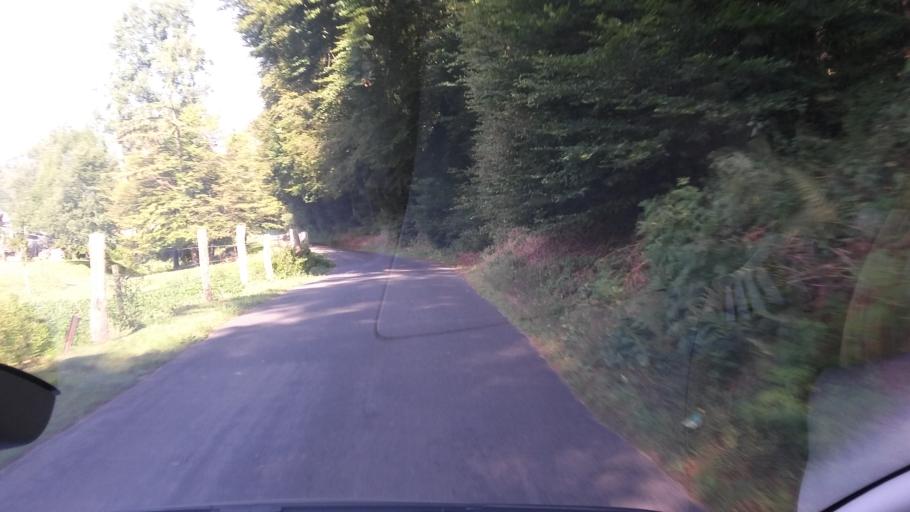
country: LU
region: Luxembourg
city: Eischen
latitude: 49.7001
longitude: 5.8574
